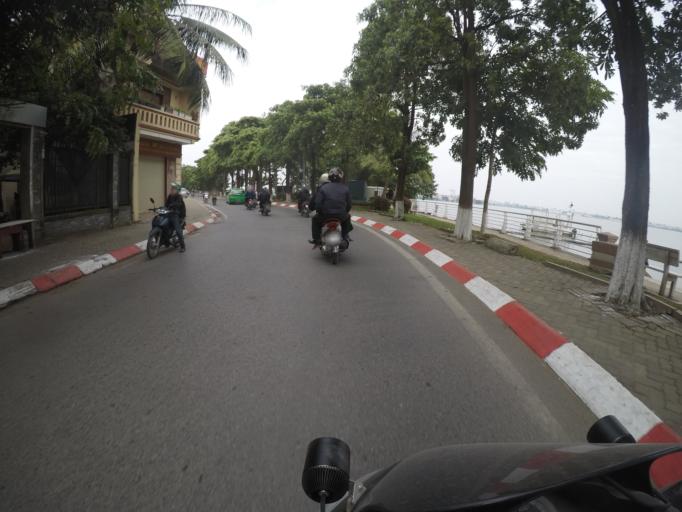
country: VN
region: Ha Noi
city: Cau Giay
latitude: 21.0479
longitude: 105.8145
